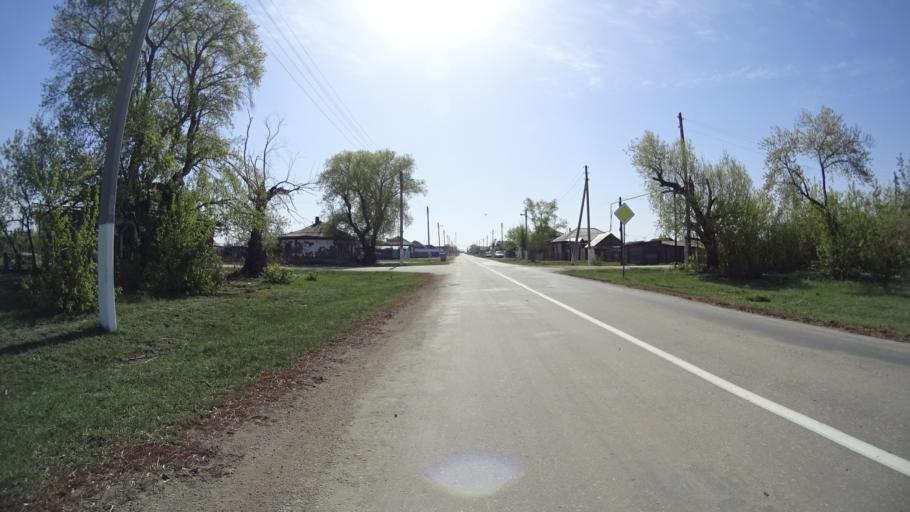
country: RU
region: Chelyabinsk
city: Chesma
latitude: 53.8012
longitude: 61.0177
